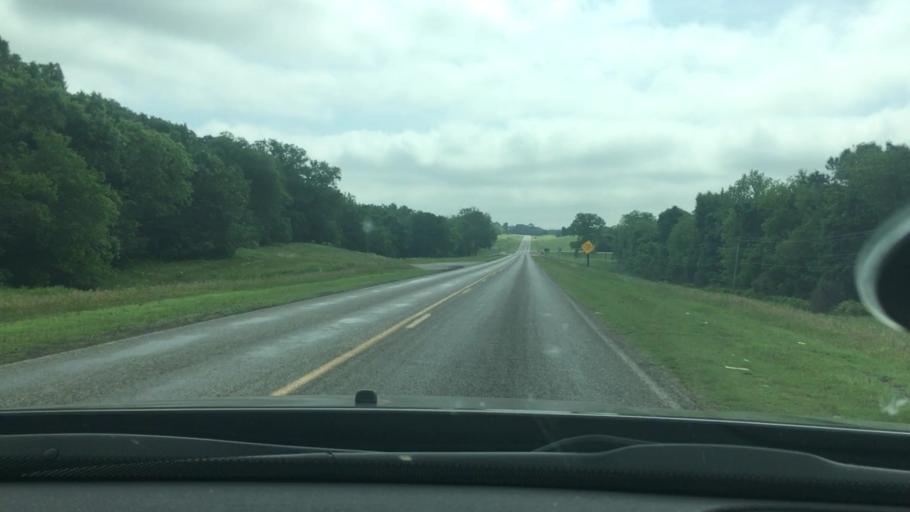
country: US
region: Oklahoma
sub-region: Johnston County
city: Tishomingo
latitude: 34.2303
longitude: -96.6405
